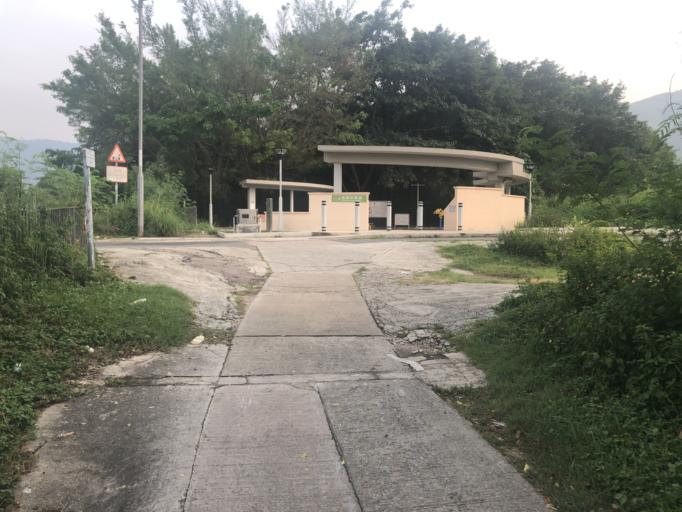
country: CN
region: Guangdong
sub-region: Shenzhen
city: Shenzhen
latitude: 22.4856
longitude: 114.1027
